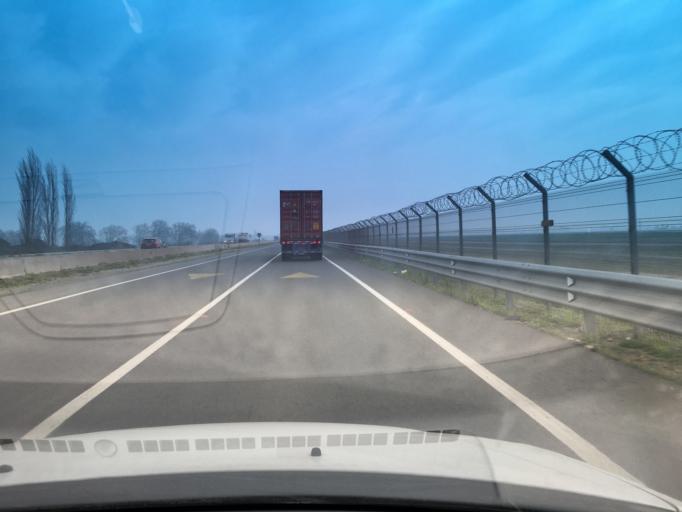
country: CL
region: Santiago Metropolitan
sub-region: Provincia de Santiago
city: Lo Prado
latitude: -33.3826
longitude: -70.8045
